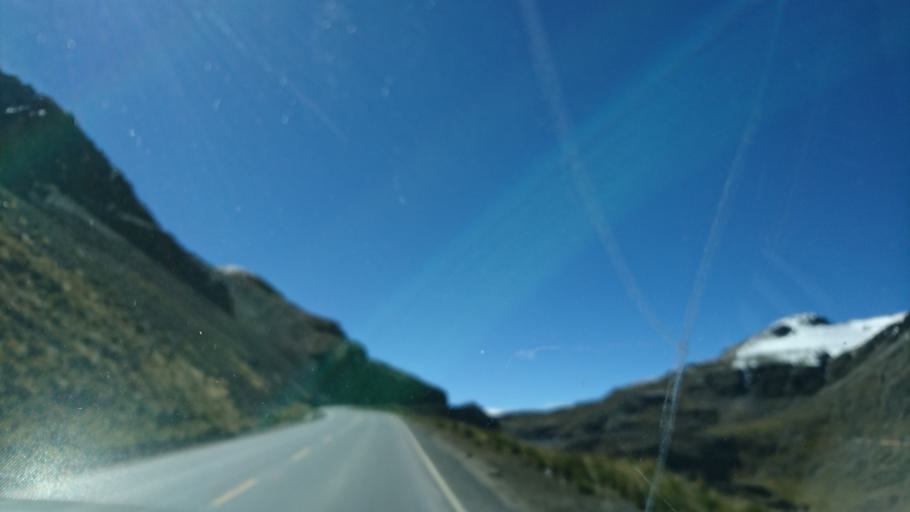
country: BO
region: La Paz
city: La Paz
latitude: -16.3901
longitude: -68.0434
